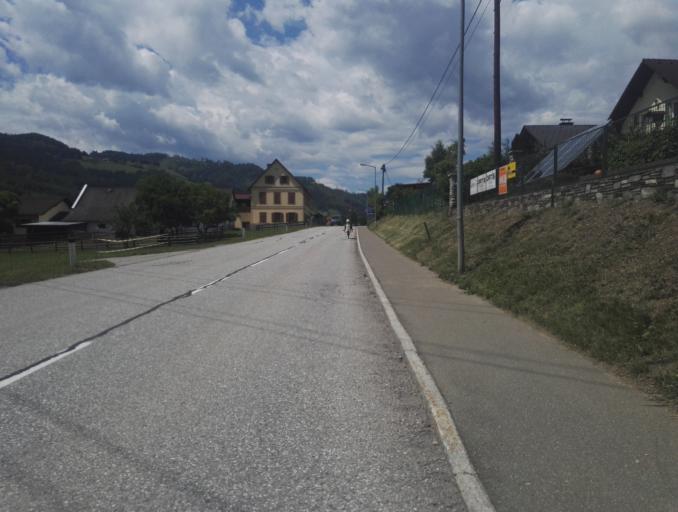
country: AT
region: Styria
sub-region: Politischer Bezirk Graz-Umgebung
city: Ubelbach
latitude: 47.2191
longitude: 15.2678
